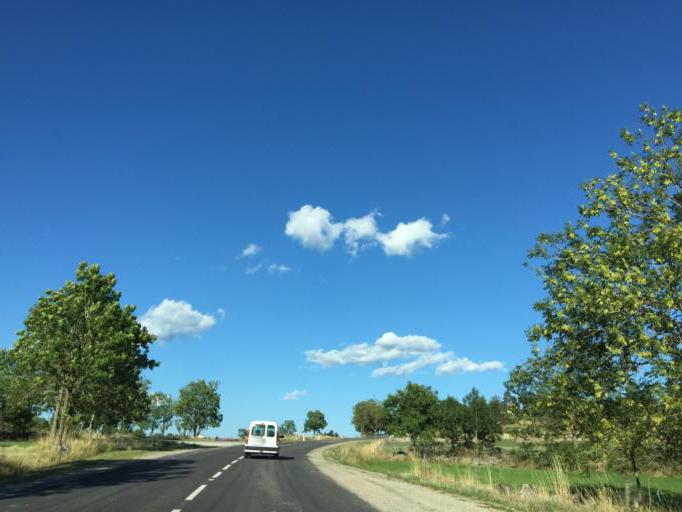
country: FR
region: Auvergne
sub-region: Departement de la Haute-Loire
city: Saugues
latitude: 44.9587
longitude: 3.5629
